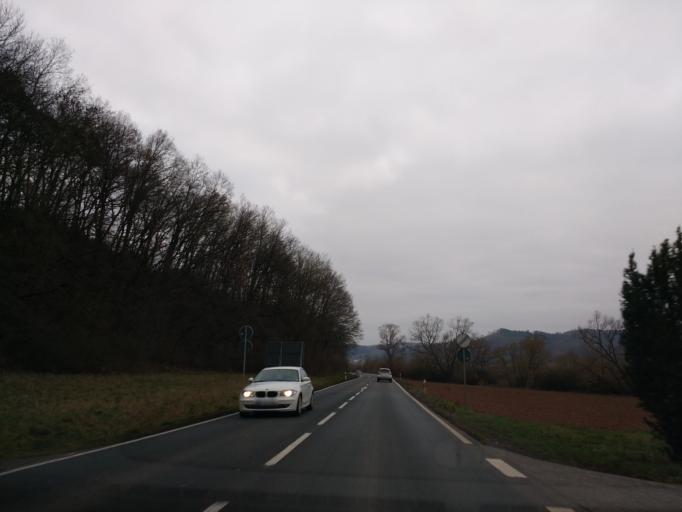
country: DE
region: Hesse
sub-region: Regierungsbezirk Kassel
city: Alheim
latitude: 51.0273
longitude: 9.6843
